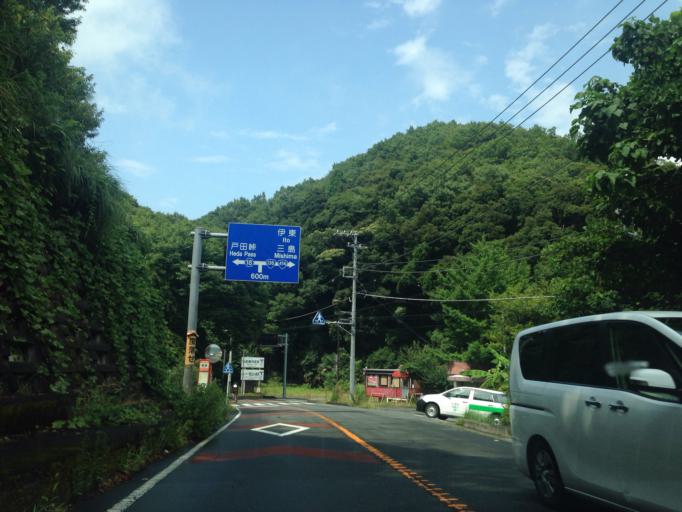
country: JP
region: Shizuoka
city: Ito
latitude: 34.9702
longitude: 138.9393
